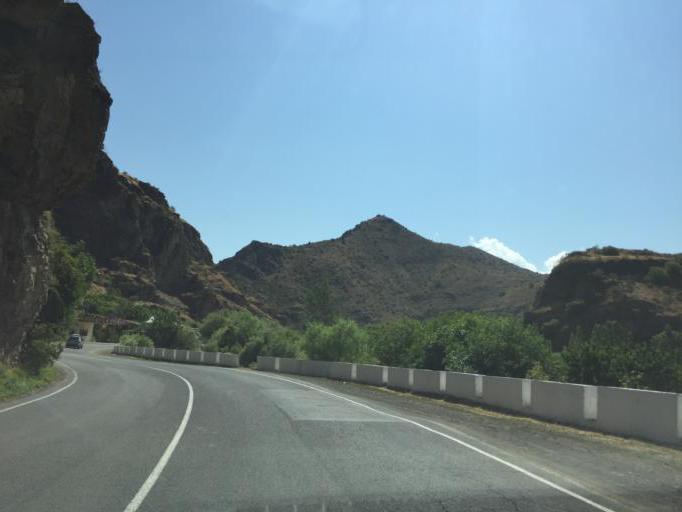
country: AM
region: Vayots' Dzori Marz
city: Vayk'
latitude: 39.6825
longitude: 45.4838
